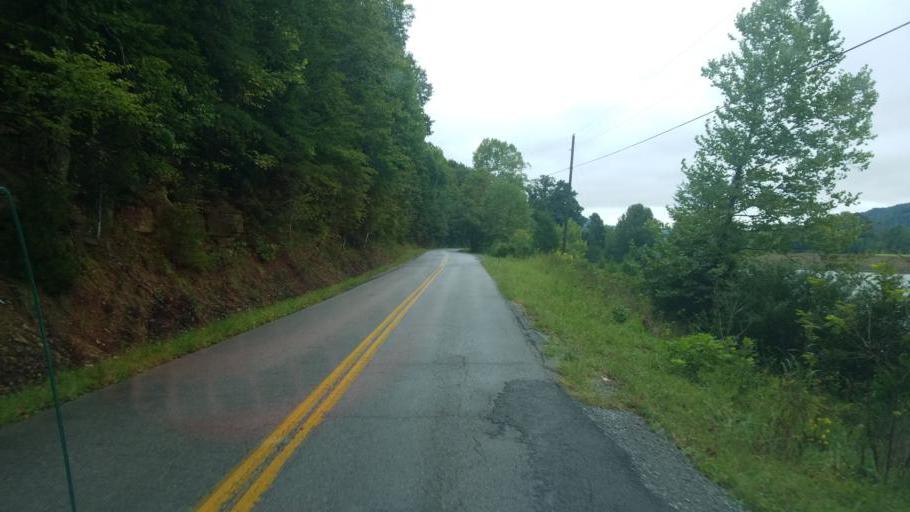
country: US
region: Kentucky
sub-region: Fleming County
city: Flemingsburg
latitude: 38.3762
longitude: -83.5408
